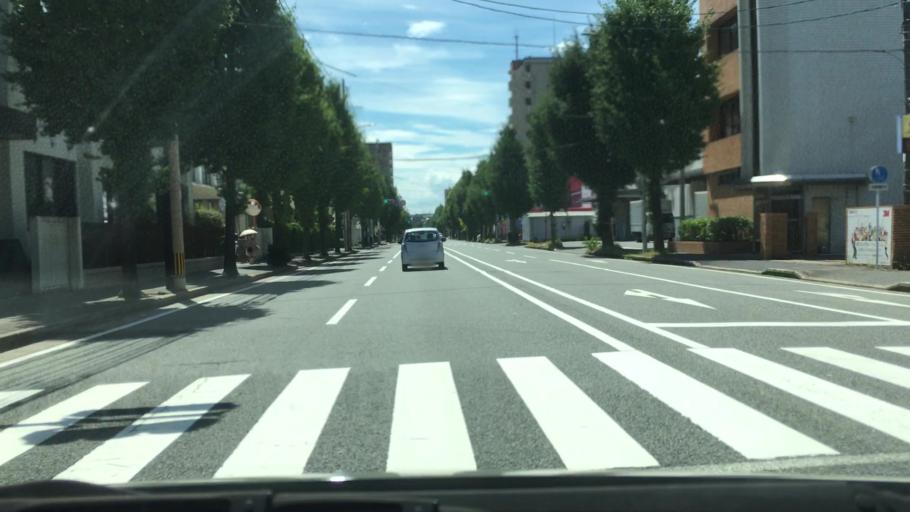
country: JP
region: Fukuoka
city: Fukuoka-shi
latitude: 33.5702
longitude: 130.4243
